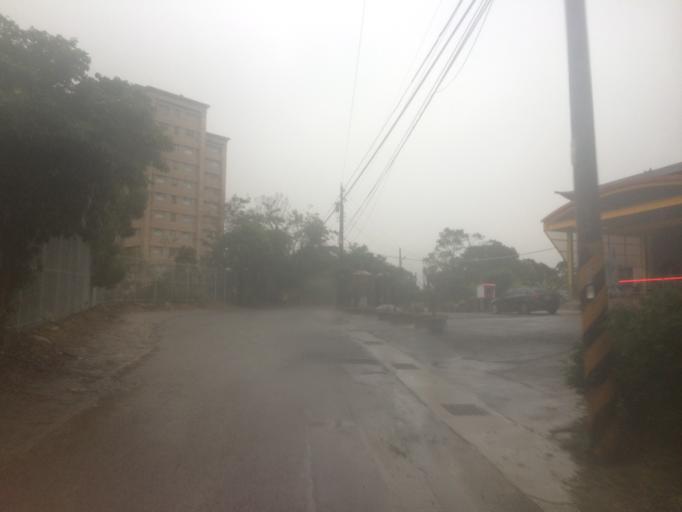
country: TW
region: Taiwan
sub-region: Hsinchu
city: Hsinchu
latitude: 24.7642
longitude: 120.9677
